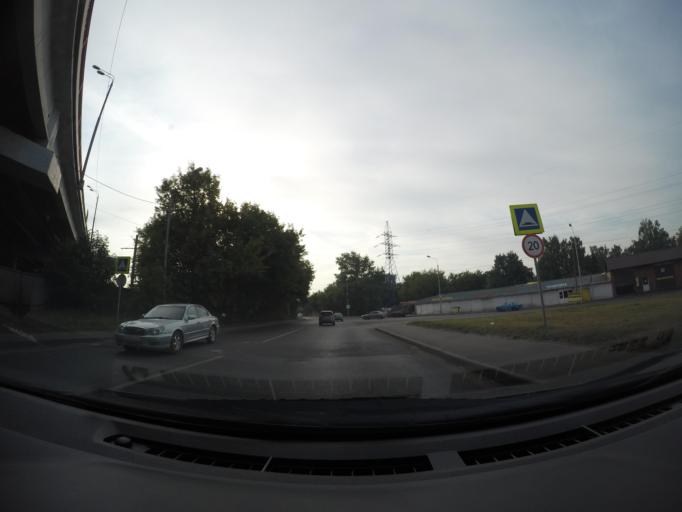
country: RU
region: Moskovskaya
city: Tomilino
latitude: 55.6604
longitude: 37.9381
